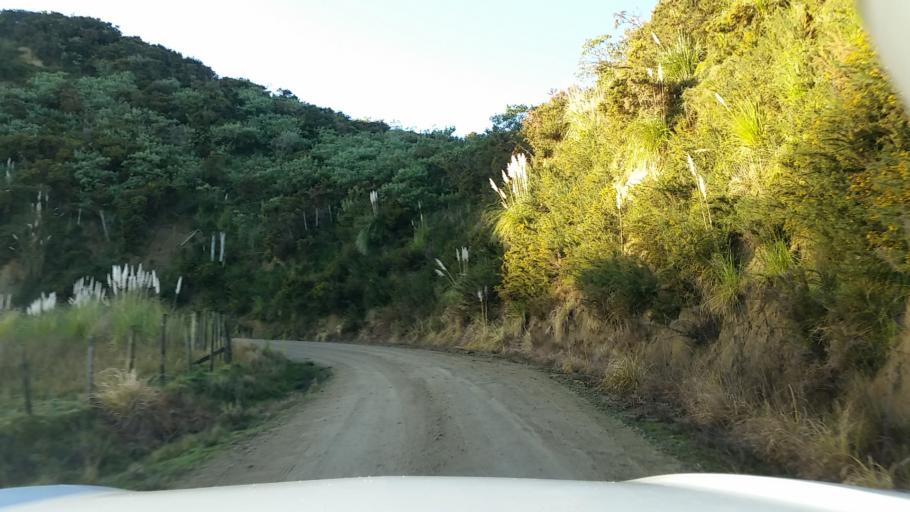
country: NZ
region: Taranaki
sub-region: South Taranaki District
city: Patea
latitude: -39.7593
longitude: 174.7365
